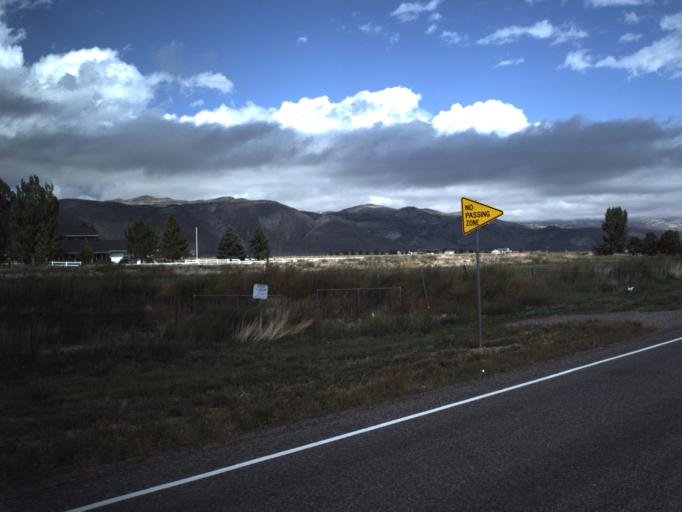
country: US
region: Utah
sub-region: Sevier County
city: Monroe
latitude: 38.6981
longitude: -112.1126
